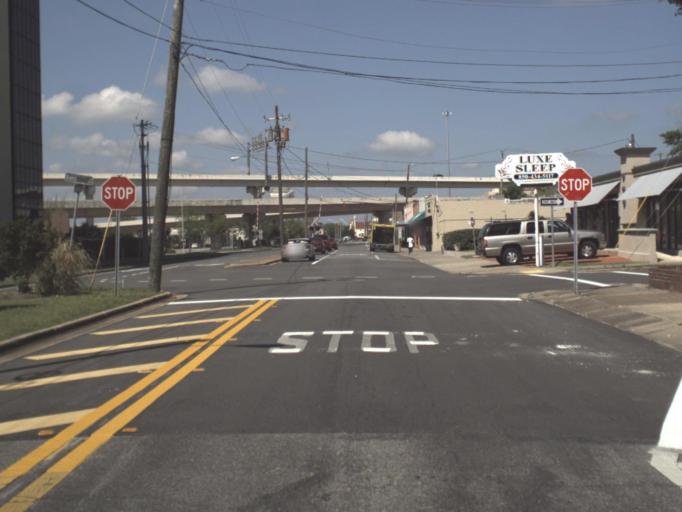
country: US
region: Florida
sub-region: Escambia County
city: Pensacola
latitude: 30.4179
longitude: -87.2096
